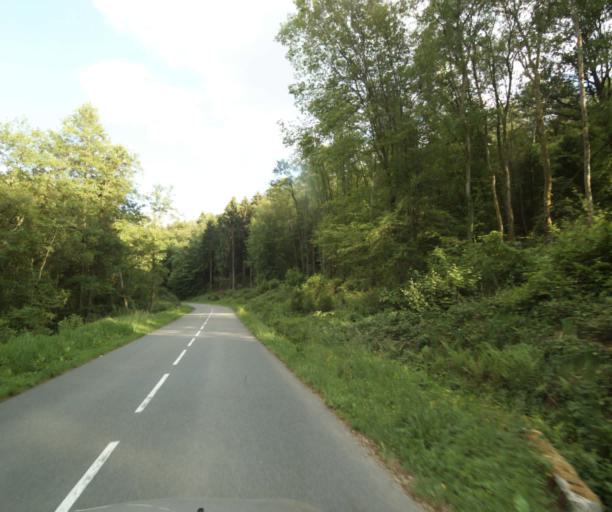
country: FR
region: Champagne-Ardenne
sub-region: Departement des Ardennes
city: Nouzonville
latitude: 49.8256
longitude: 4.7080
